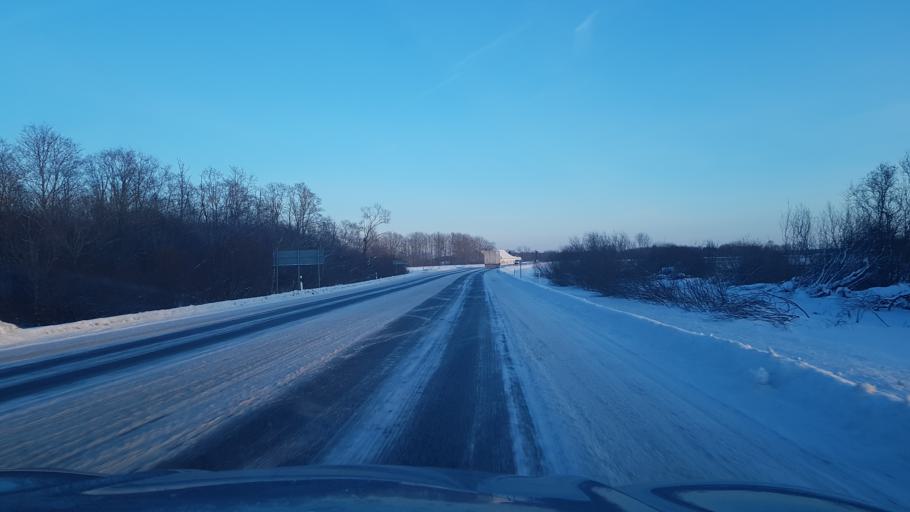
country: EE
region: Ida-Virumaa
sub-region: Narva-Joesuu linn
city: Narva-Joesuu
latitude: 59.4009
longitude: 28.0648
